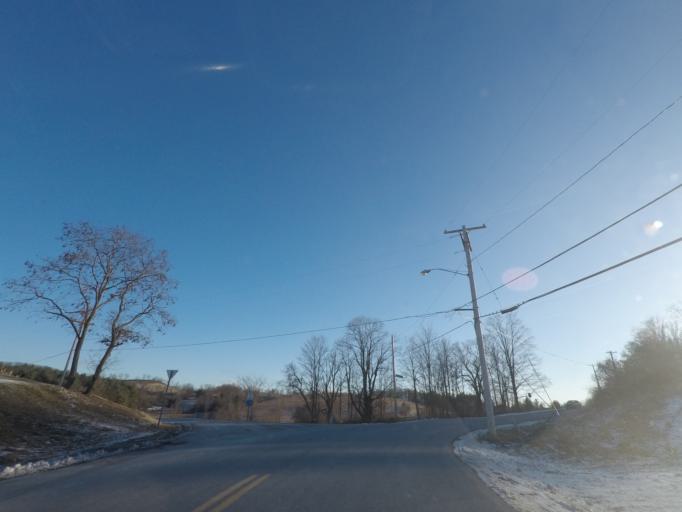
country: US
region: New York
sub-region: Rensselaer County
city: Poestenkill
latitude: 42.7261
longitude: -73.5964
